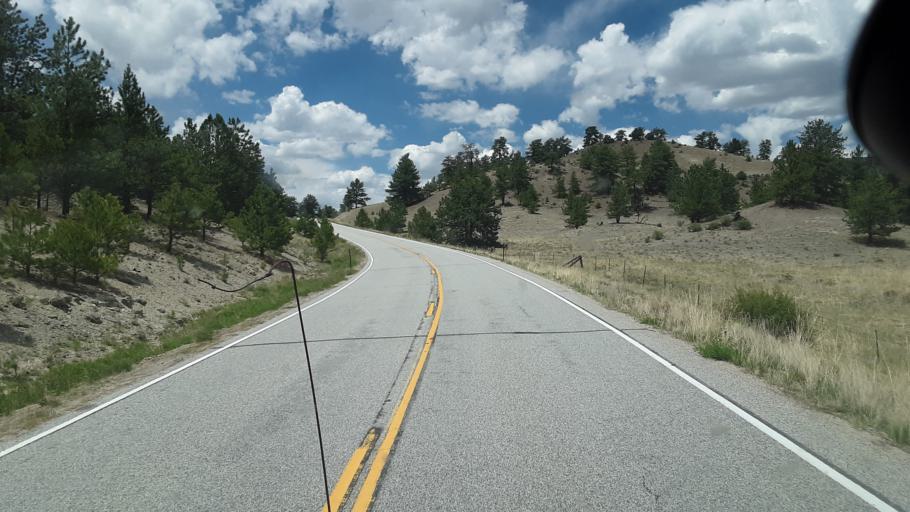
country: US
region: Colorado
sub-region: Teller County
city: Cripple Creek
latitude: 38.7696
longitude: -105.5650
